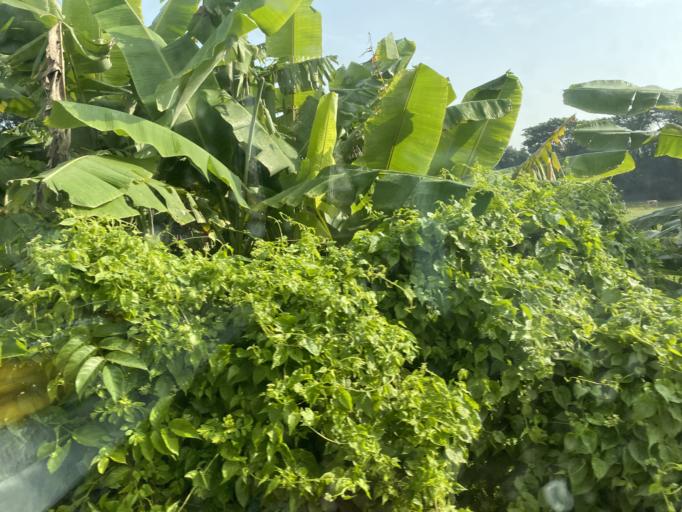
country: BD
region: Chittagong
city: Nabinagar
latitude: 23.9617
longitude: 91.1184
